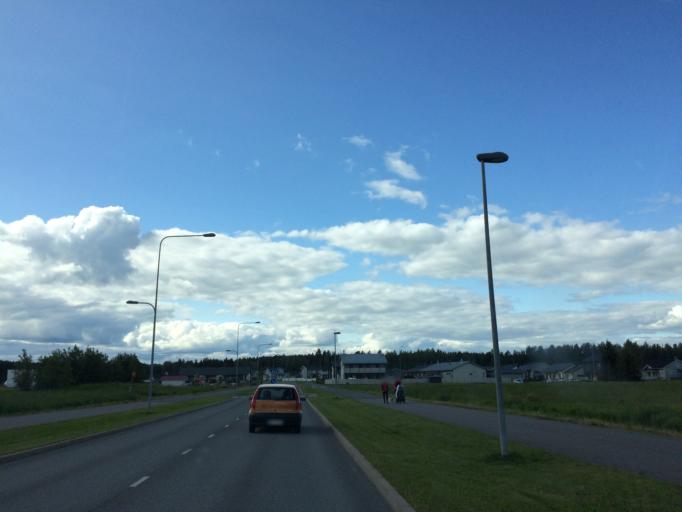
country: FI
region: Haeme
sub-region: Haemeenlinna
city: Parola
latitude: 60.9744
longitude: 24.3799
